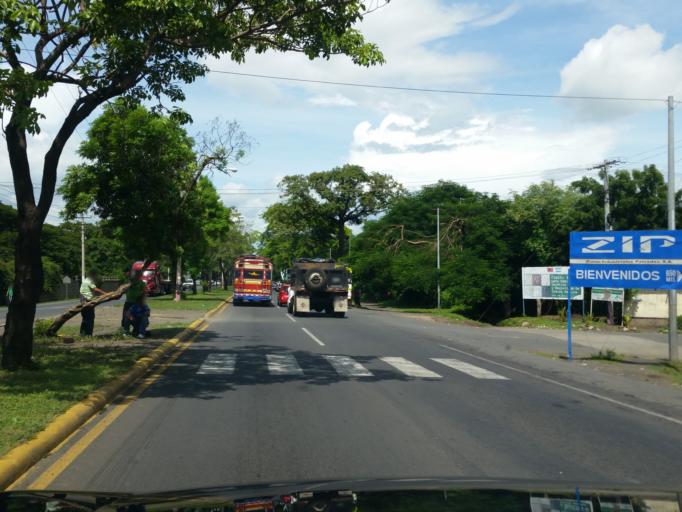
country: NI
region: Managua
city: Tipitapa
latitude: 12.1539
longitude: -86.1471
